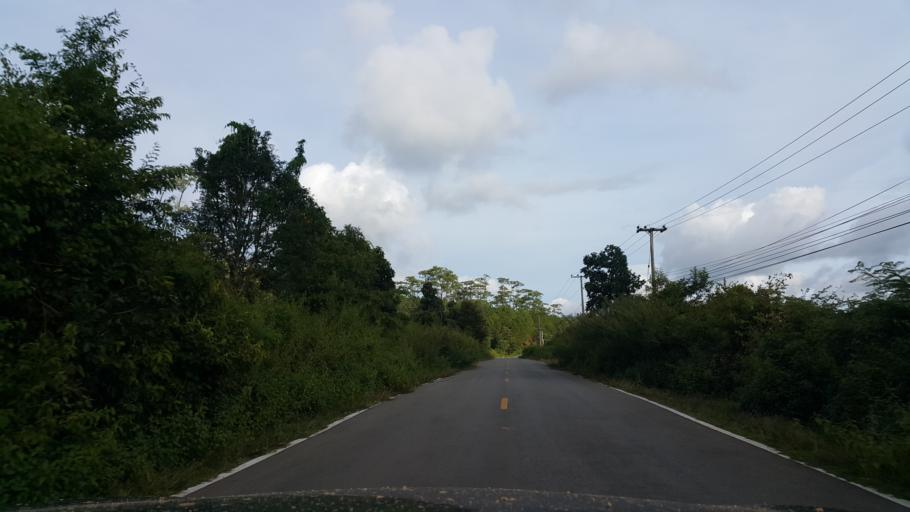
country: TH
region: Chiang Mai
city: Chaem Luang
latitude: 19.0825
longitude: 98.3260
